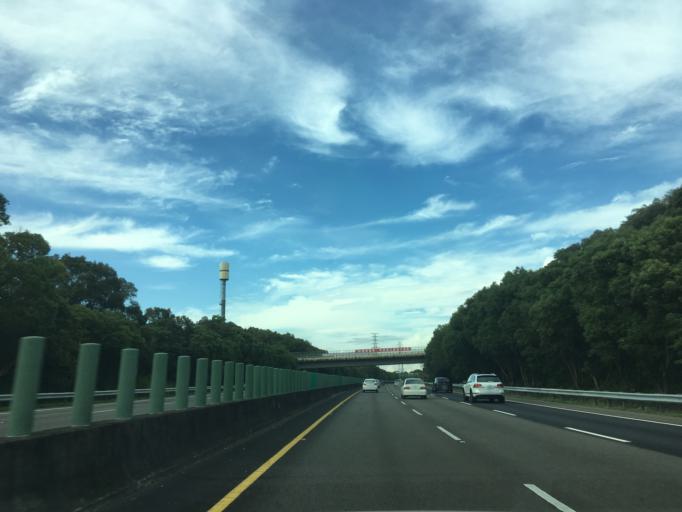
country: TW
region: Taiwan
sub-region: Chiayi
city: Jiayi Shi
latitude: 23.5802
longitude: 120.5099
